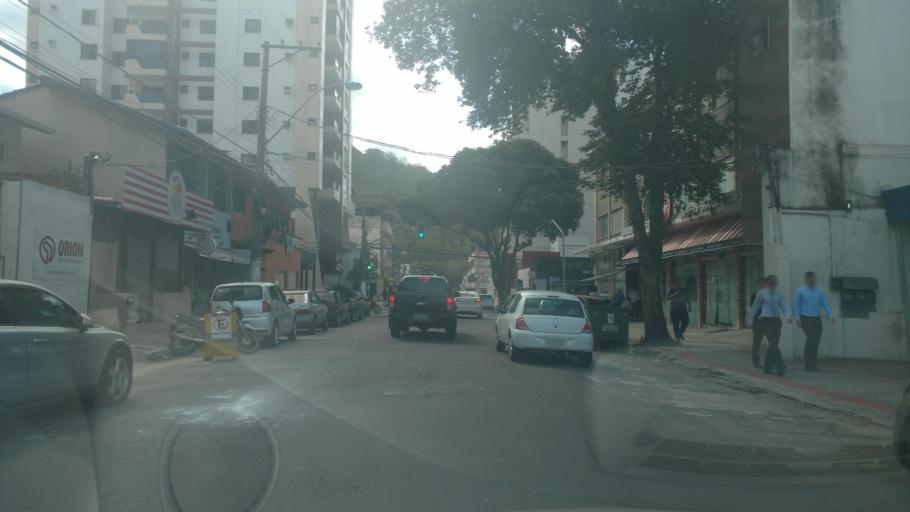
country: BR
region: Espirito Santo
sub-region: Vila Velha
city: Vila Velha
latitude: -20.3355
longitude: -40.2871
